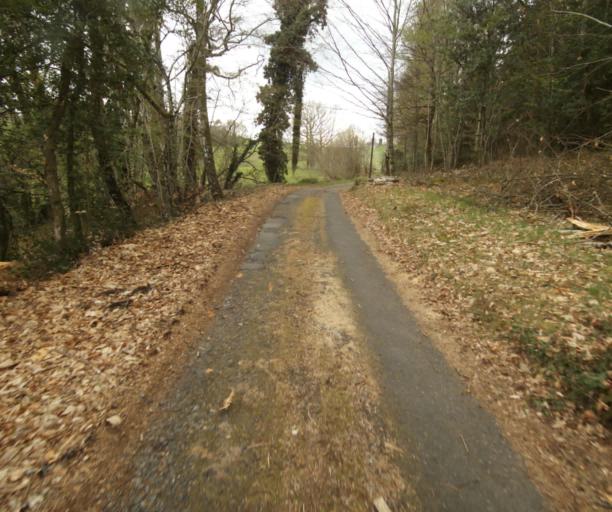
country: FR
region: Limousin
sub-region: Departement de la Correze
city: Laguenne
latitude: 45.2504
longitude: 1.8680
